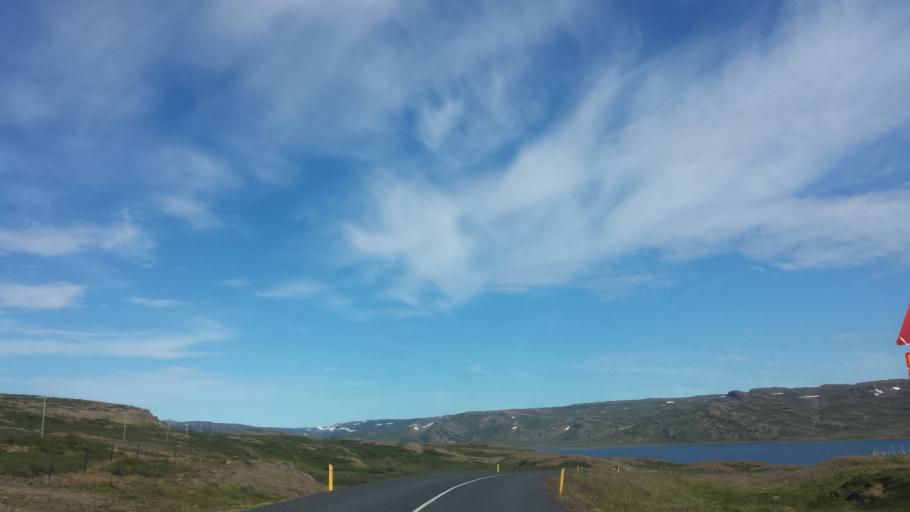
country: IS
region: West
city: Stykkisholmur
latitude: 65.7419
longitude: -21.7088
